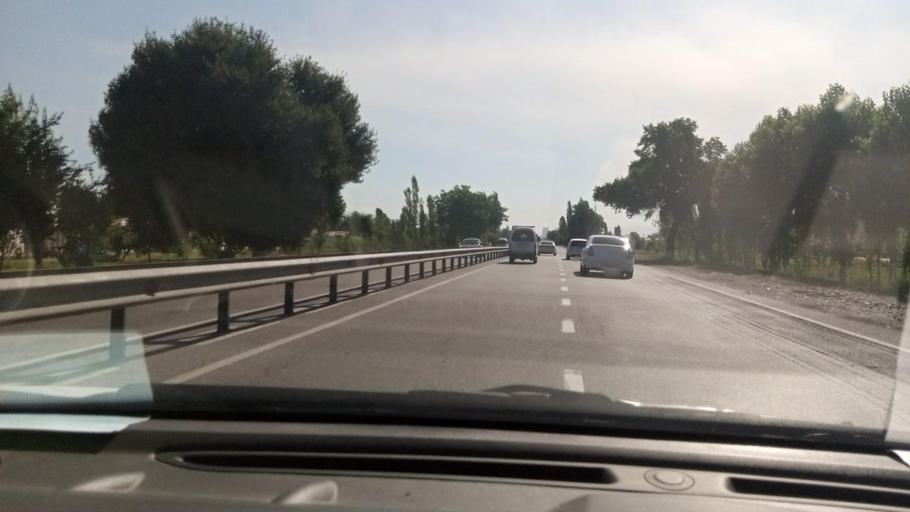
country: UZ
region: Toshkent
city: Ohangaron
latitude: 40.9062
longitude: 69.7361
